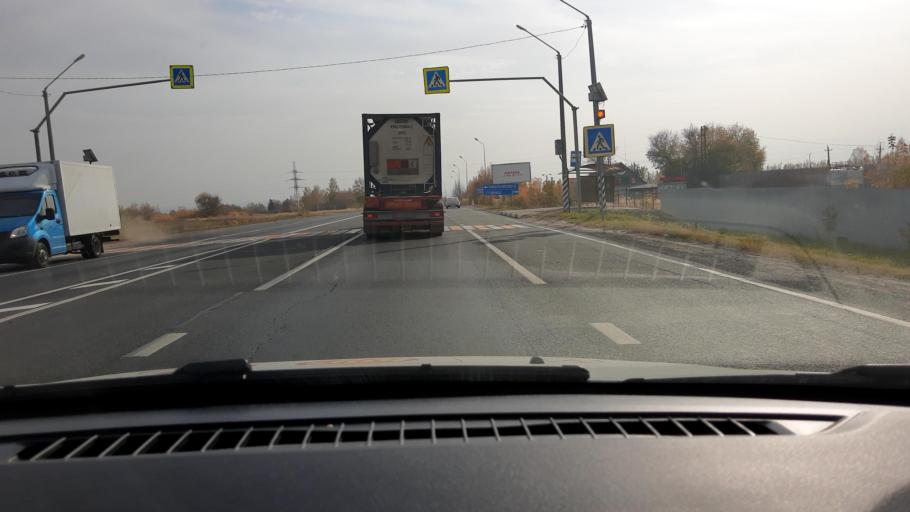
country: RU
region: Nizjnij Novgorod
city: Kstovo
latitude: 56.1117
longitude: 44.2825
